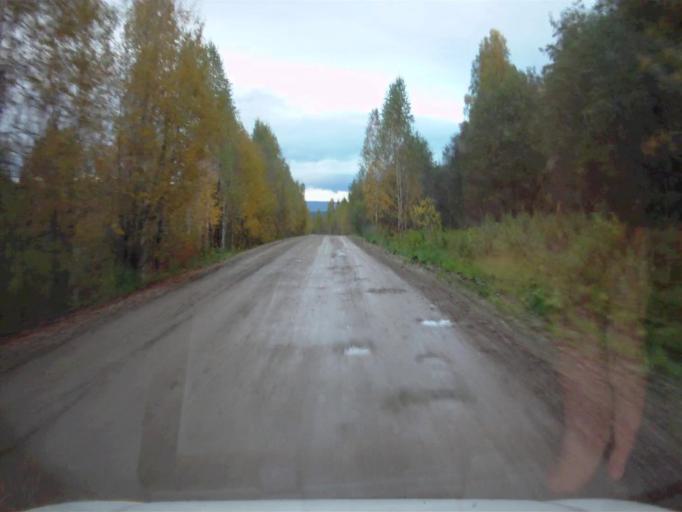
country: RU
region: Sverdlovsk
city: Mikhaylovsk
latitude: 56.1934
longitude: 59.1949
